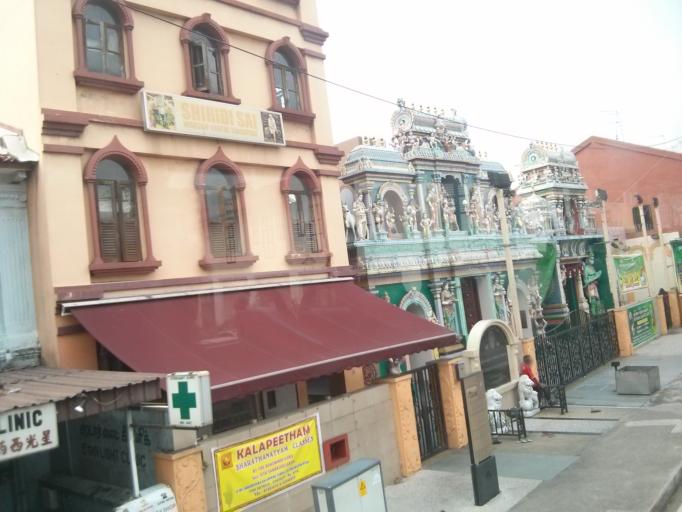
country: SG
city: Singapore
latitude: 1.3151
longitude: 103.8579
